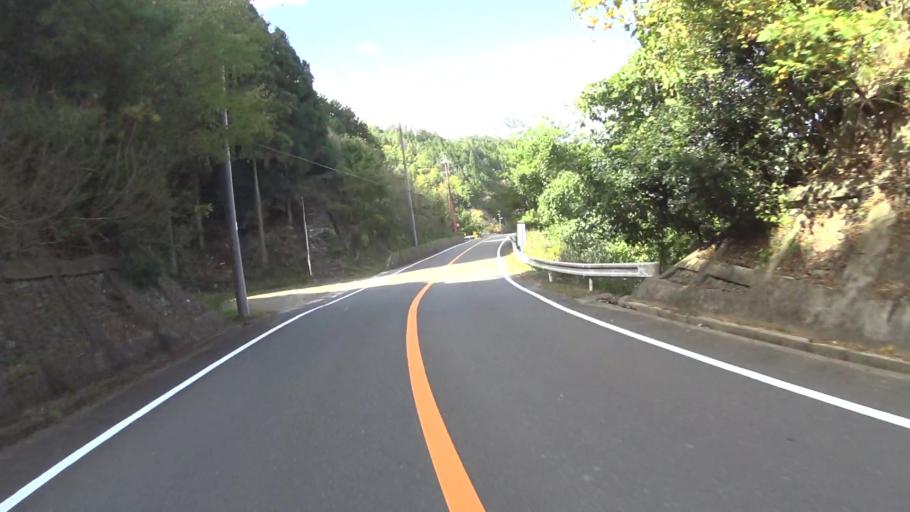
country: JP
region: Kyoto
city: Kameoka
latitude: 35.1299
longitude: 135.5447
